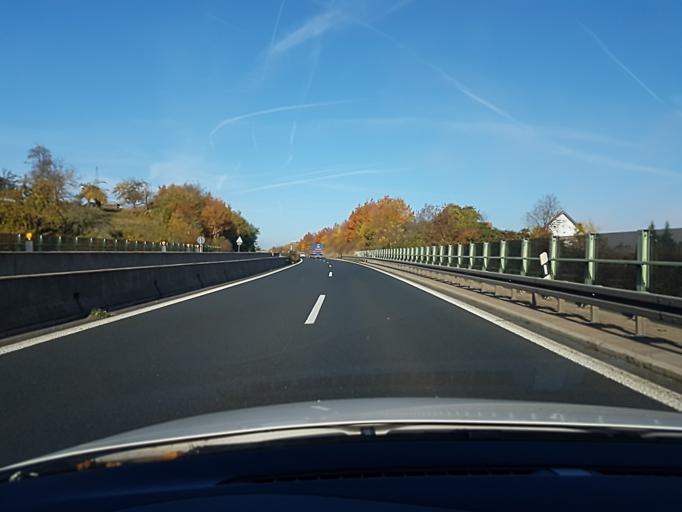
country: DE
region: Bavaria
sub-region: Regierungsbezirk Unterfranken
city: Klingenberg am Main
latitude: 49.7700
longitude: 9.1758
